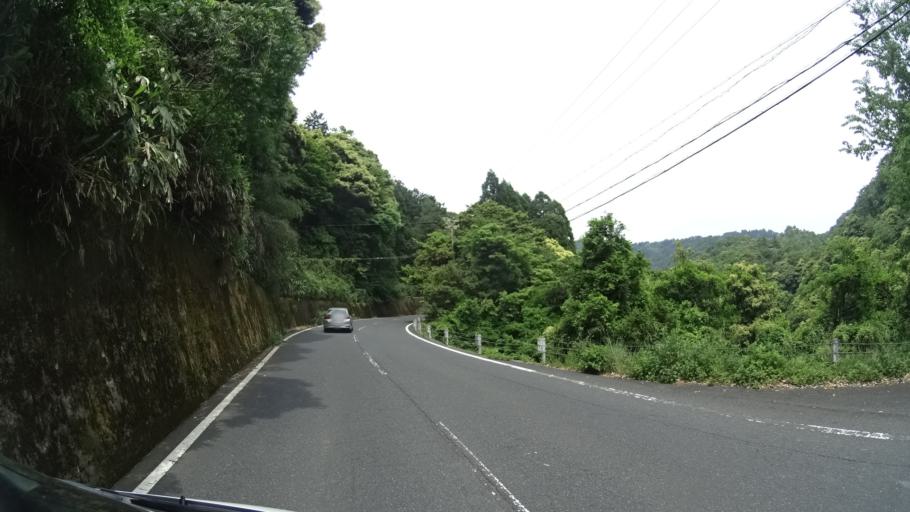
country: JP
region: Kyoto
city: Miyazu
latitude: 35.7048
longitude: 135.2823
